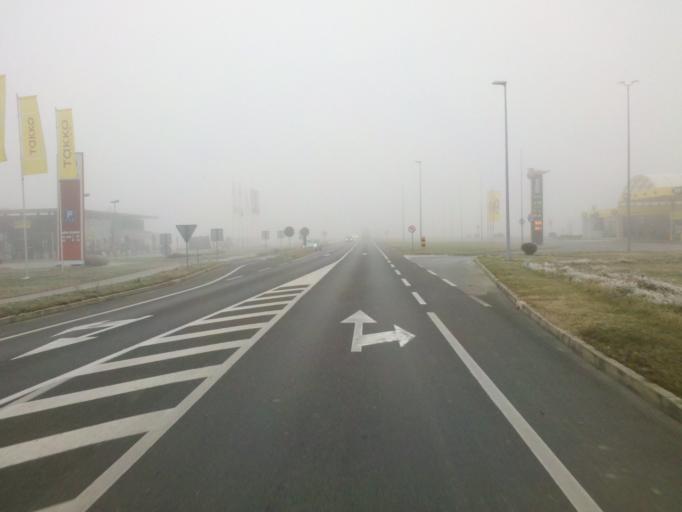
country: HR
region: Varazdinska
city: Sracinec
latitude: 46.3202
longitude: 16.3077
